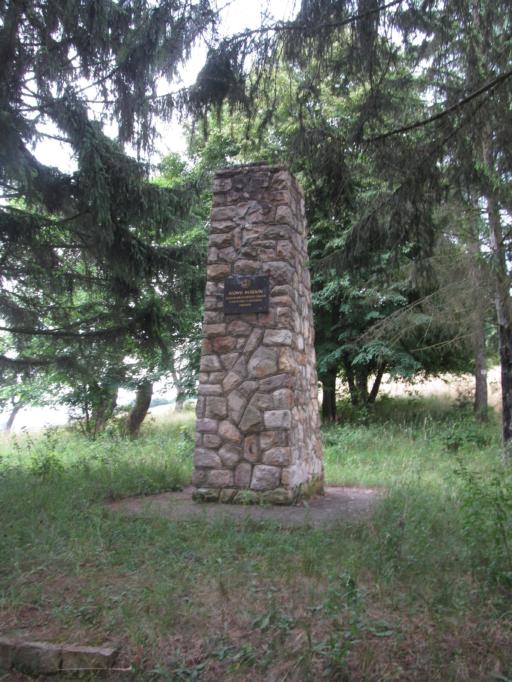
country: HU
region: Borsod-Abauj-Zemplen
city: Jardanhaza
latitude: 48.2126
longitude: 20.1614
